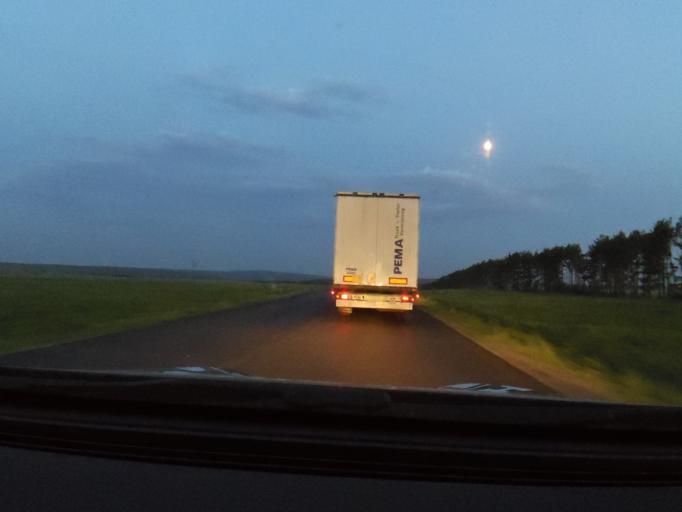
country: RU
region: Bashkortostan
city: Duvan
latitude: 56.0379
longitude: 58.2088
